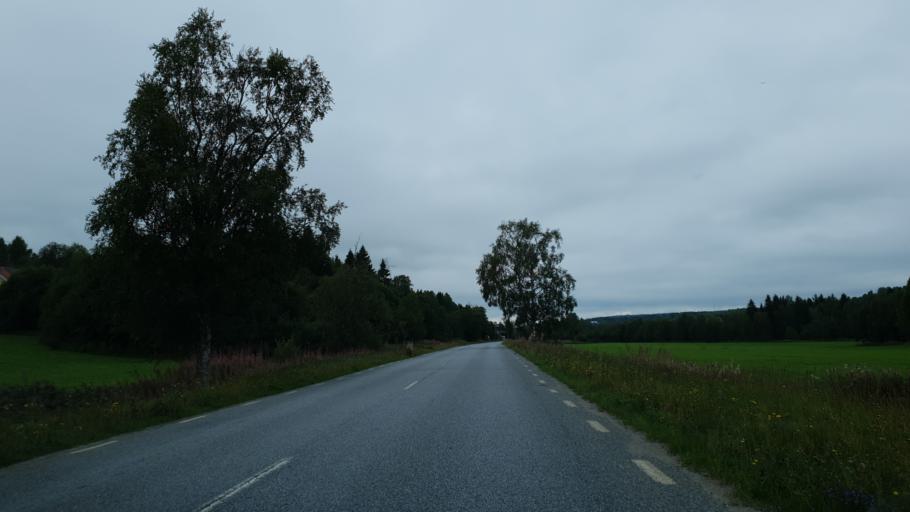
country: SE
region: Vaesterbotten
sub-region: Skelleftea Kommun
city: Burea
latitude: 64.3918
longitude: 21.2950
